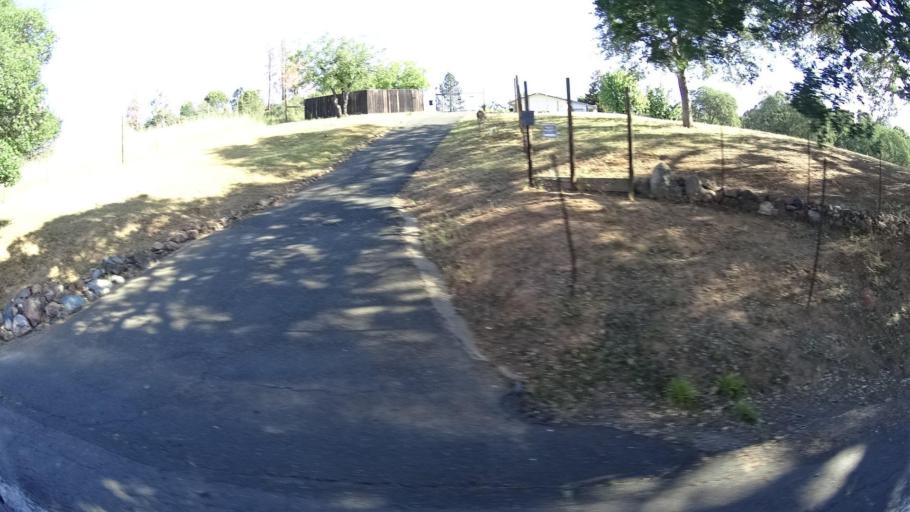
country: US
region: California
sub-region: Lake County
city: Lakeport
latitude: 39.0422
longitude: -122.9472
